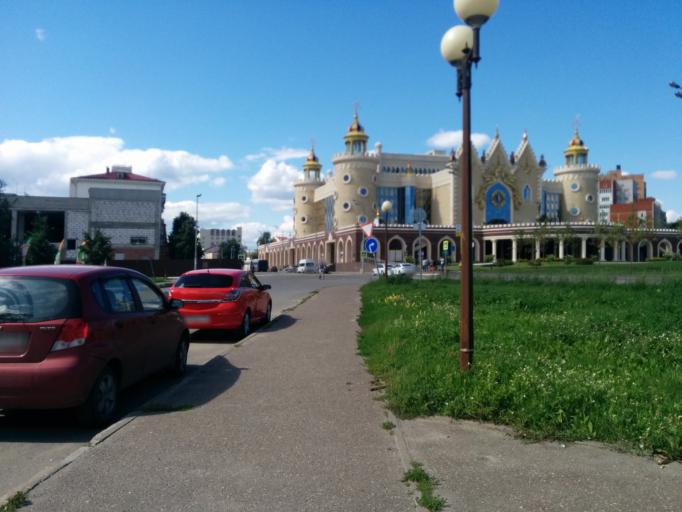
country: RU
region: Tatarstan
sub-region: Gorod Kazan'
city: Kazan
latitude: 55.7785
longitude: 49.1391
